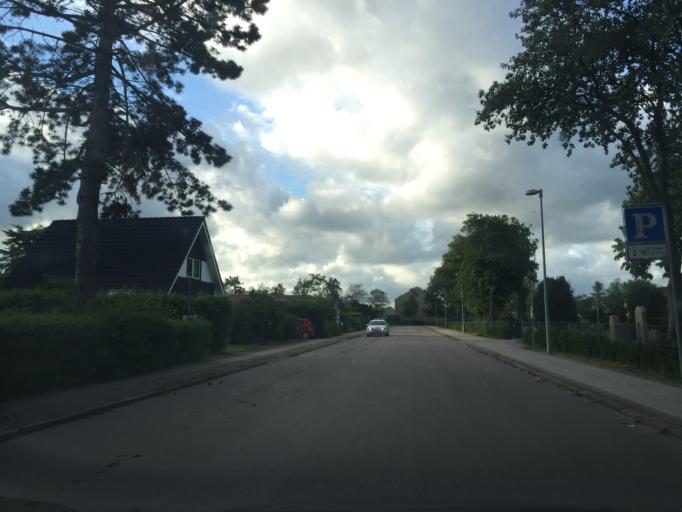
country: DK
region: Capital Region
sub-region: Hoje-Taastrup Kommune
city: Taastrup
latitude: 55.6545
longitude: 12.3031
